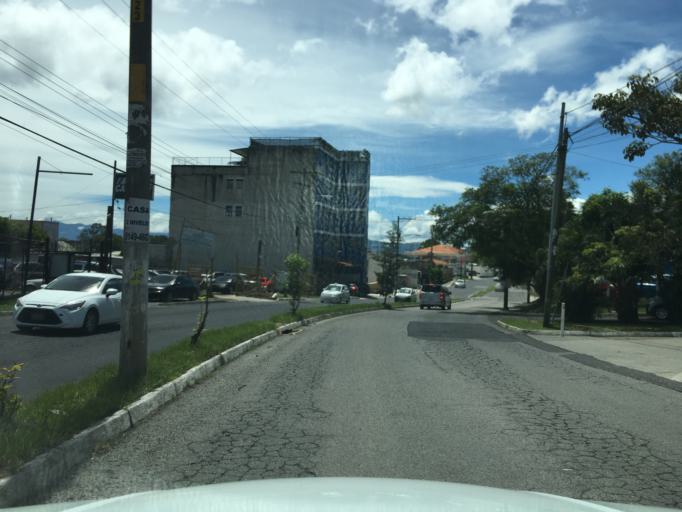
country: GT
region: Guatemala
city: Guatemala City
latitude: 14.6451
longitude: -90.5579
